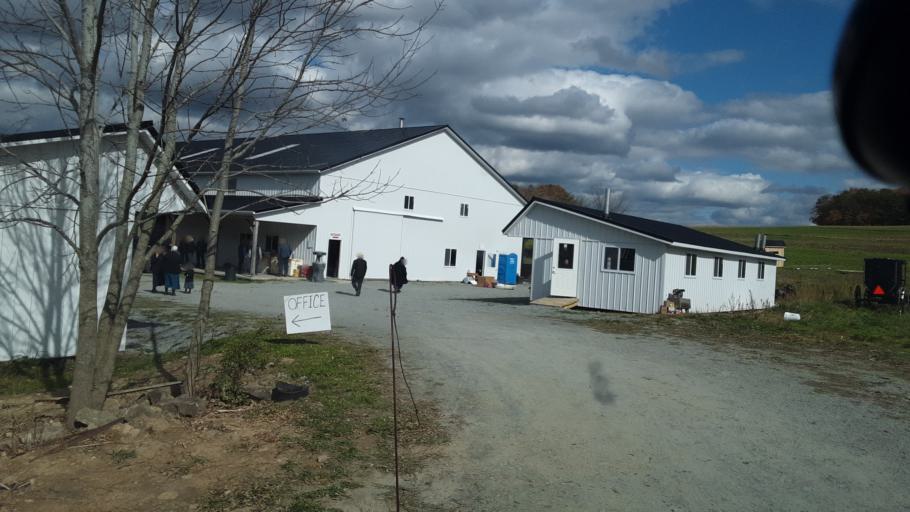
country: US
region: New York
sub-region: Allegany County
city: Andover
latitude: 41.9805
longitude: -77.7611
